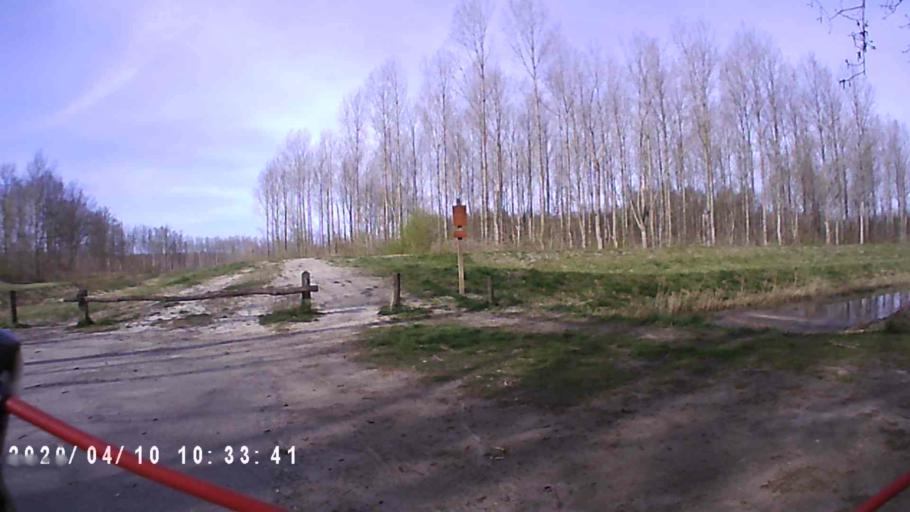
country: NL
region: Friesland
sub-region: Gemeente Dongeradeel
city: Anjum
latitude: 53.3913
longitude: 6.2128
